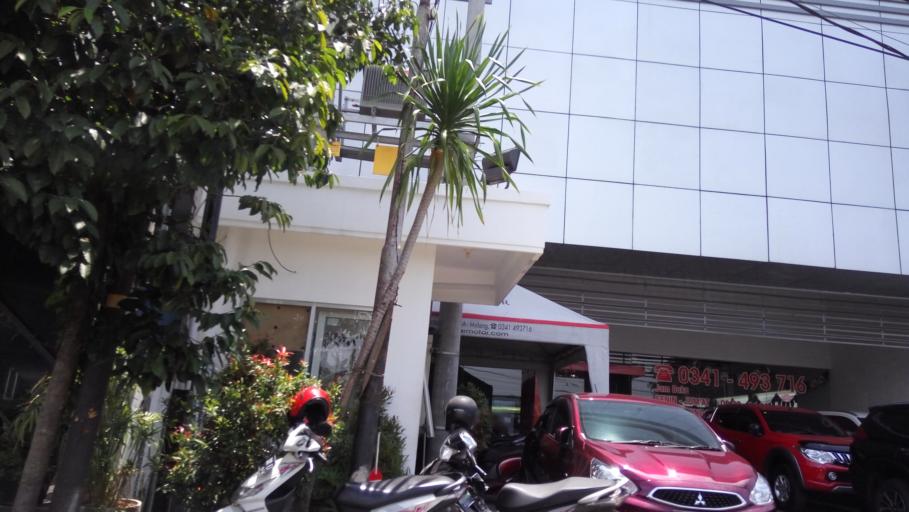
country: ID
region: East Java
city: Malang
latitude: -7.9461
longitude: 112.6405
